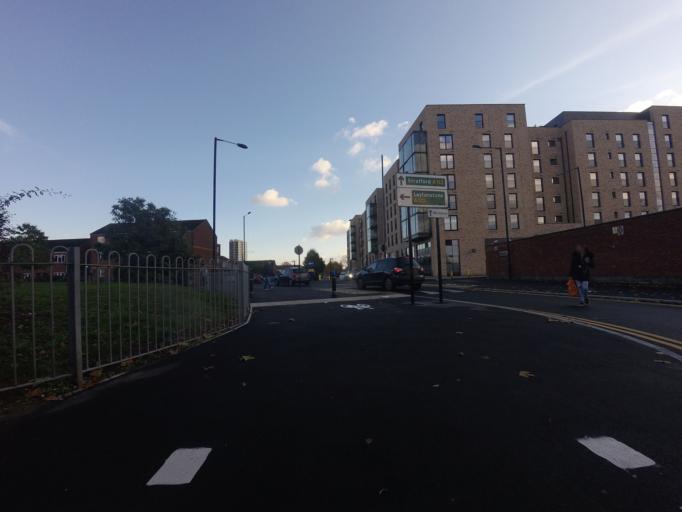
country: GB
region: England
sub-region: Greater London
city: Poplar
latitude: 51.5493
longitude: -0.0035
